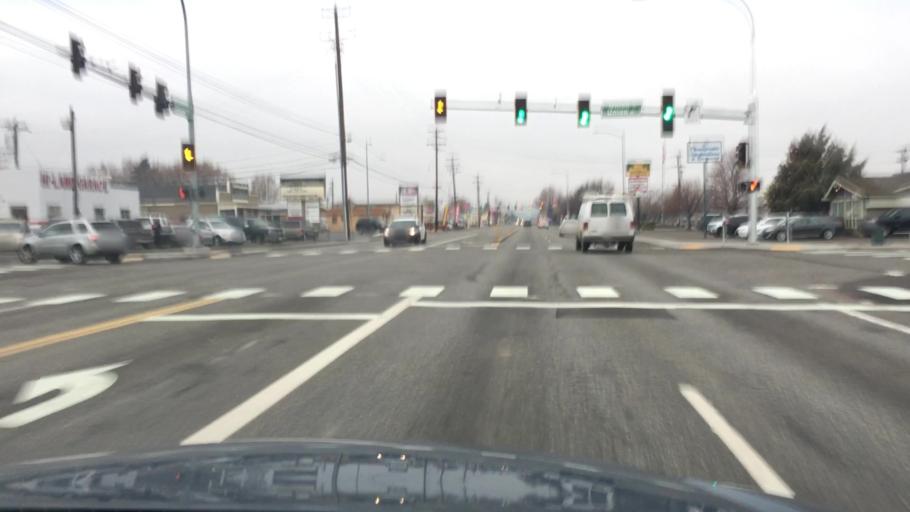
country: US
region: Washington
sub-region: Franklin County
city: West Pasco
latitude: 46.2124
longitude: -119.1795
